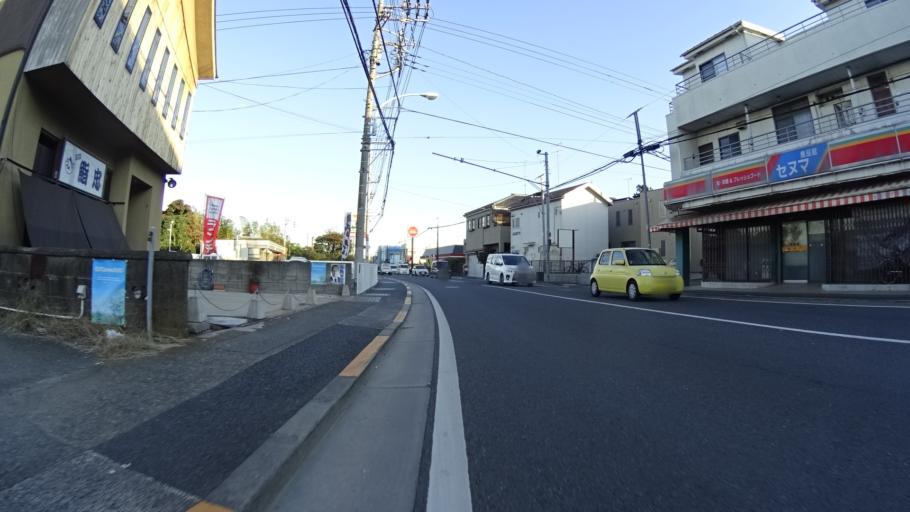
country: JP
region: Tokyo
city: Hachioji
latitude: 35.6642
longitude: 139.3052
